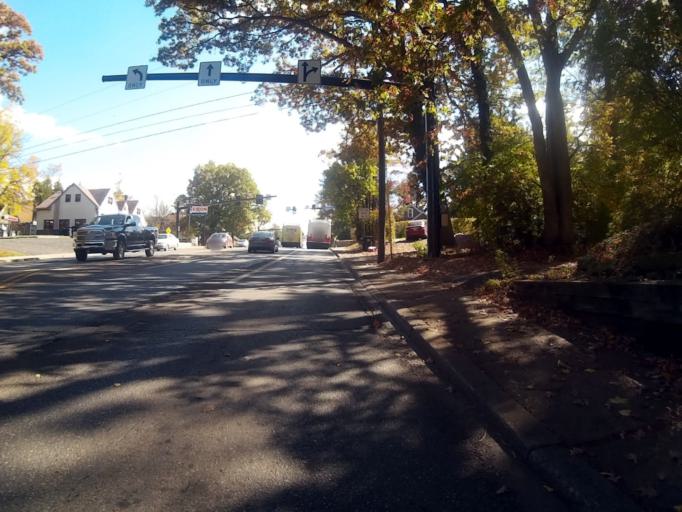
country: US
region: Pennsylvania
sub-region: Centre County
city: State College
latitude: 40.7989
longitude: -77.8759
